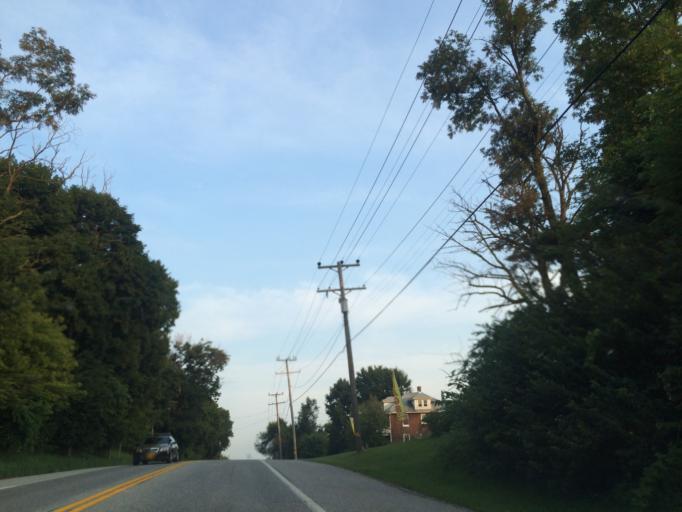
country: US
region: Maryland
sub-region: Carroll County
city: Westminster
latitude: 39.6348
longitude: -77.0041
